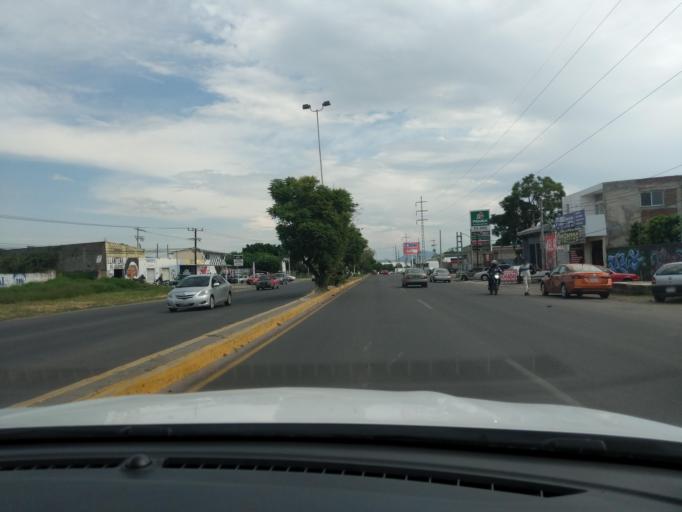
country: MX
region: Jalisco
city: San Jose del Castillo
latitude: 20.5113
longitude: -103.2365
